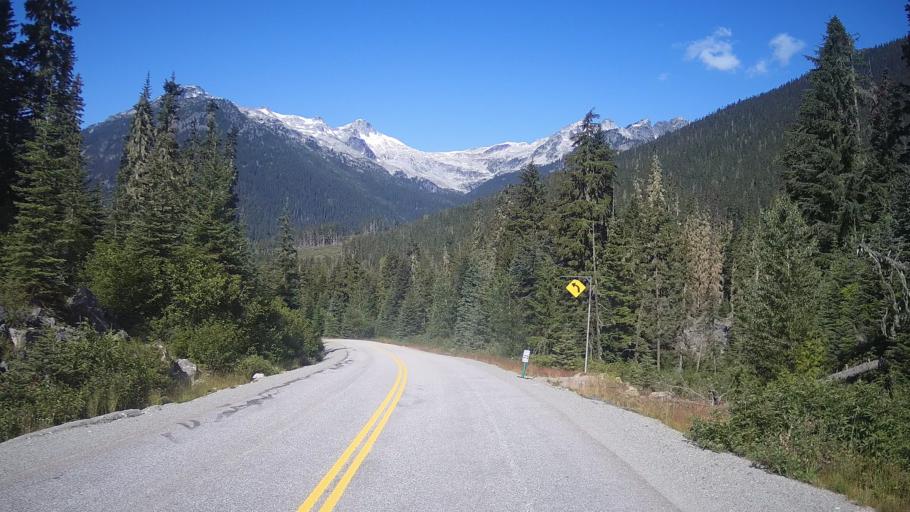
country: CA
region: British Columbia
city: Pemberton
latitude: 50.3662
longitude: -122.5160
